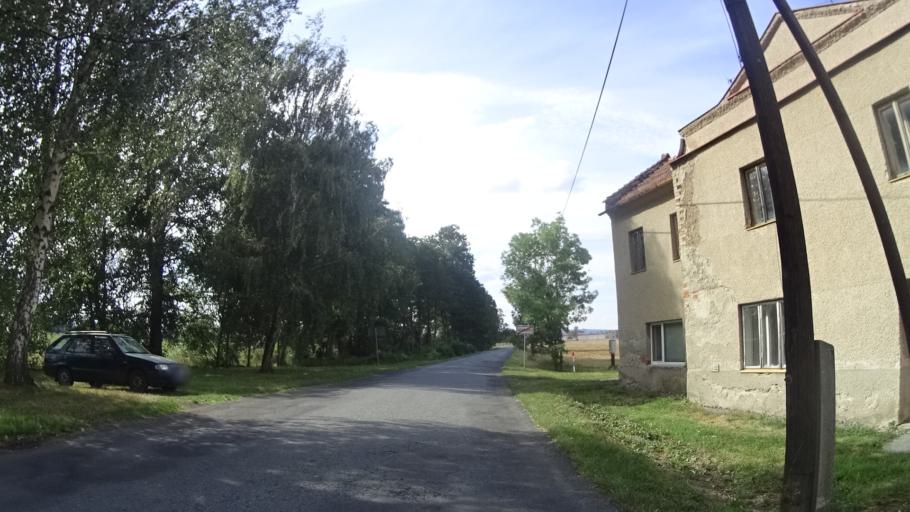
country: CZ
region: Olomoucky
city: Moravicany
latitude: 49.7491
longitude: 16.9726
